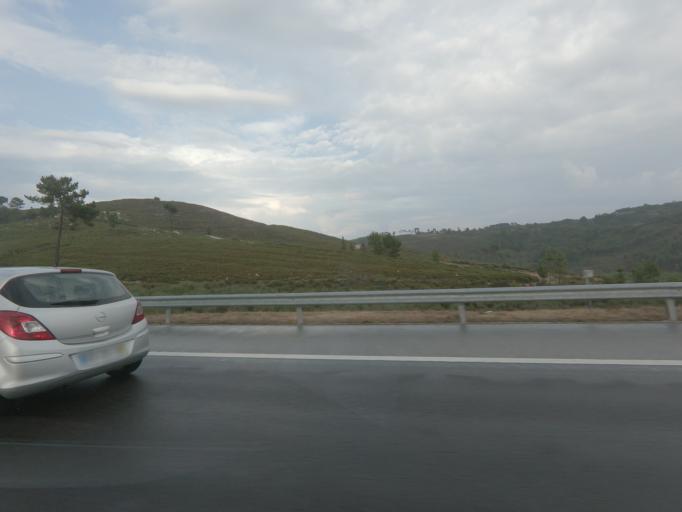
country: PT
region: Viseu
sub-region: Viseu
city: Campo
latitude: 40.7520
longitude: -7.9229
